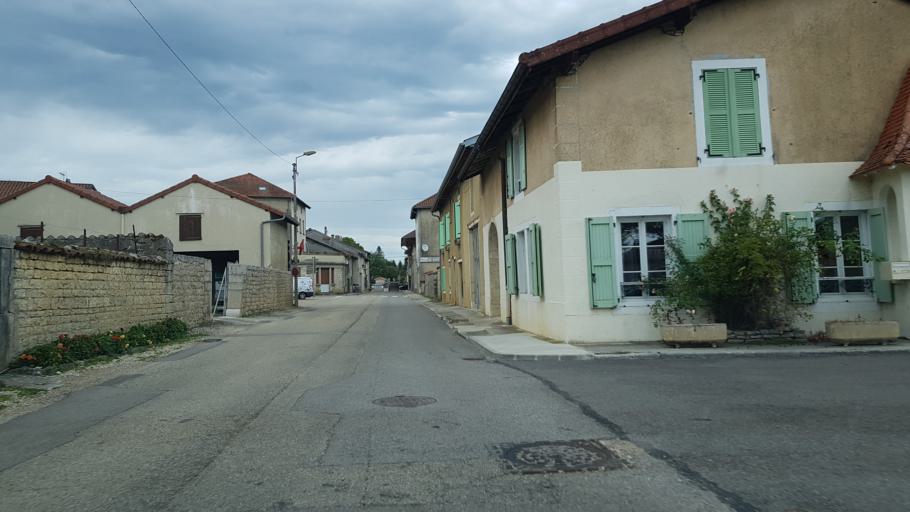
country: FR
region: Rhone-Alpes
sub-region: Departement de l'Ain
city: Cuisiat
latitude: 46.2628
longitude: 5.4256
